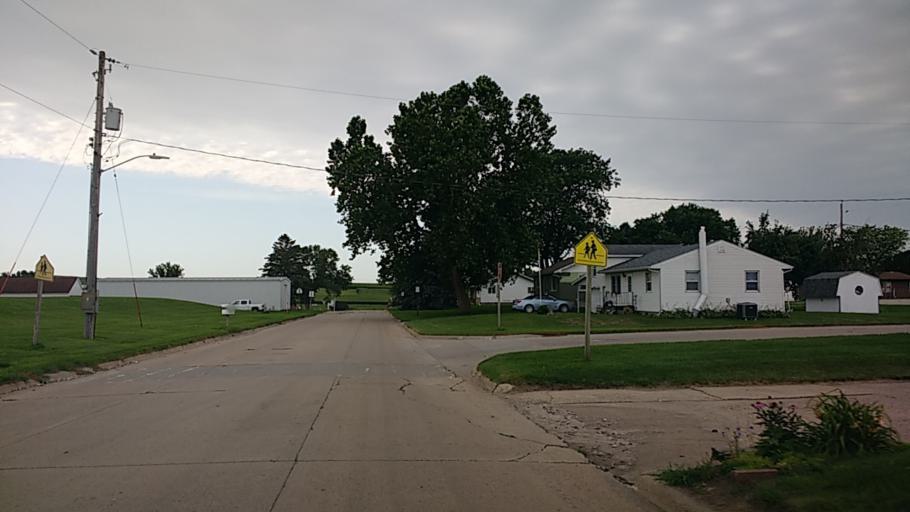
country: US
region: Iowa
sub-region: Woodbury County
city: Moville
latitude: 42.4837
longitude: -96.0653
